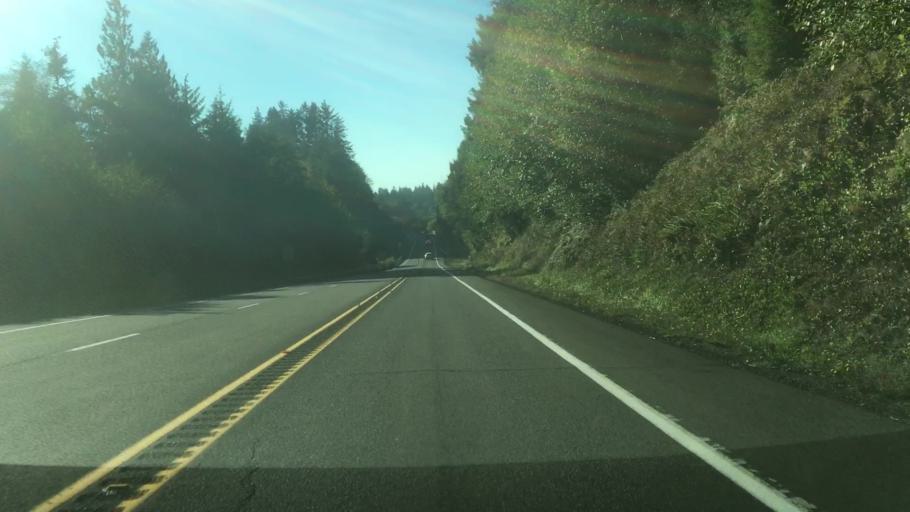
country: US
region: Washington
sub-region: Pacific County
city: South Bend
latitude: 46.6796
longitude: -123.8960
